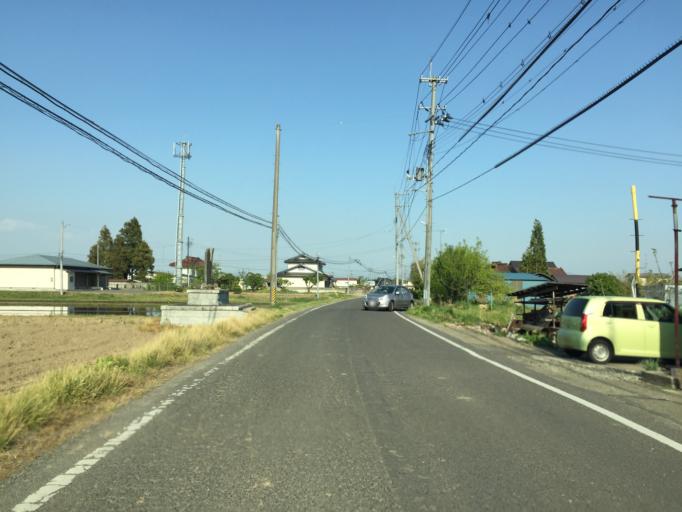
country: JP
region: Fukushima
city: Koriyama
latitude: 37.4065
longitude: 140.3250
